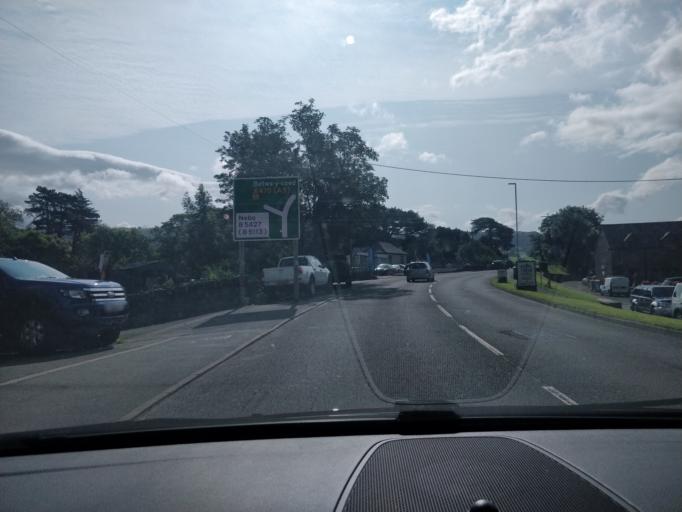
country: GB
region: Wales
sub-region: Conwy
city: Llanrwst
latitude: 53.1367
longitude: -3.7957
